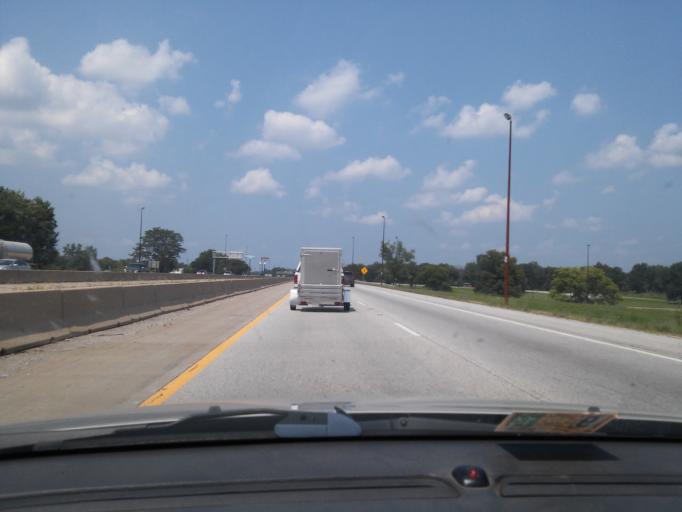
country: US
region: Illinois
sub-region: Sangamon County
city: Grandview
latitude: 39.7837
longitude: -89.6000
